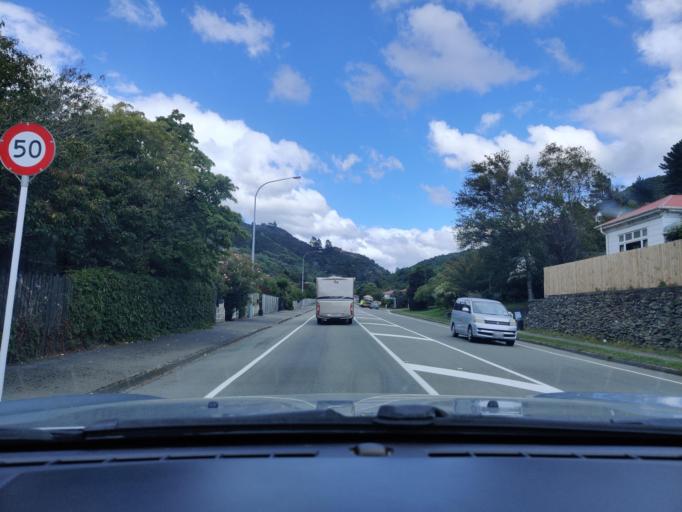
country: NZ
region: Marlborough
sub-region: Marlborough District
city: Picton
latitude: -41.2988
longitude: 173.9992
